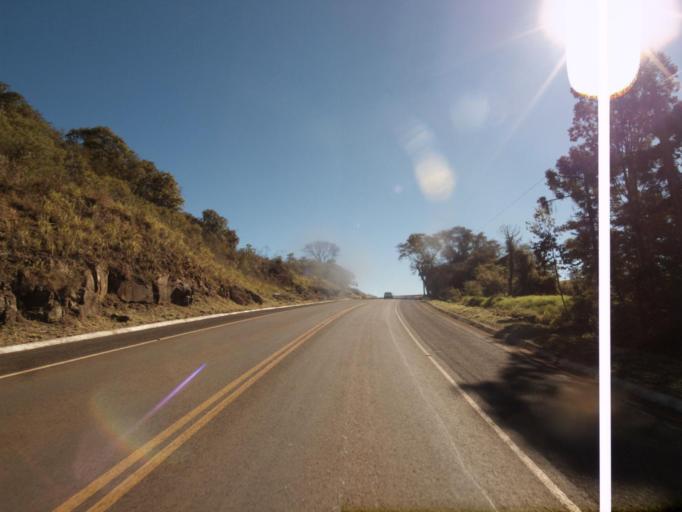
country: AR
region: Misiones
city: Bernardo de Irigoyen
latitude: -26.6181
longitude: -53.6610
